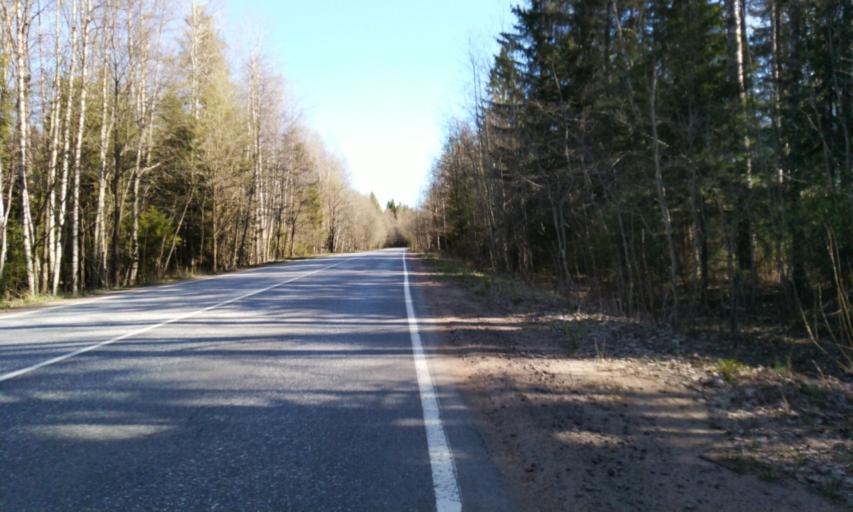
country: RU
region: Leningrad
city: Garbolovo
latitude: 60.3426
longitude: 30.4370
